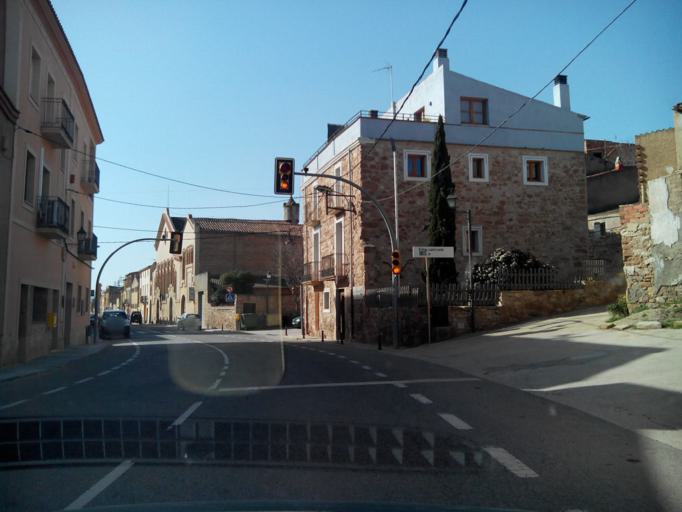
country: ES
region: Catalonia
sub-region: Provincia de Tarragona
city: Blancafort
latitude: 41.4243
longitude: 1.2023
